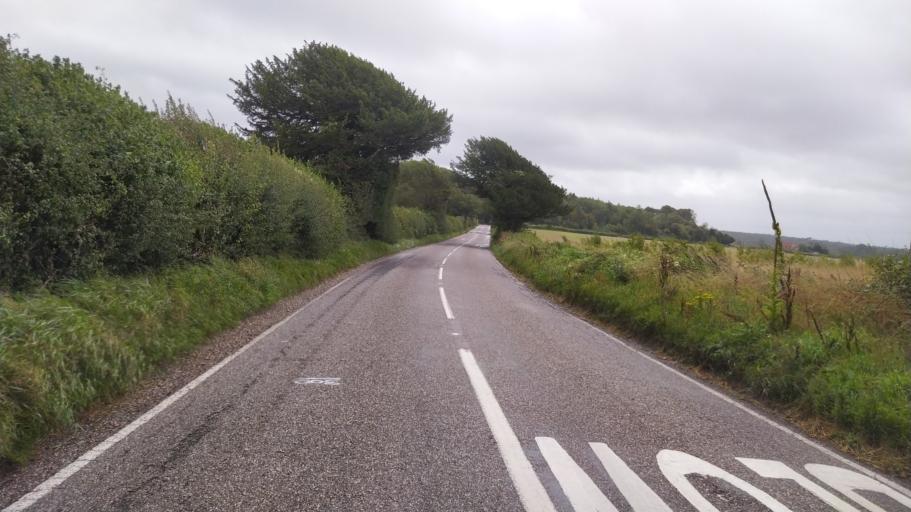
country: GB
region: England
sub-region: Wiltshire
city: Bower Chalke
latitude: 50.9208
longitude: -1.9447
